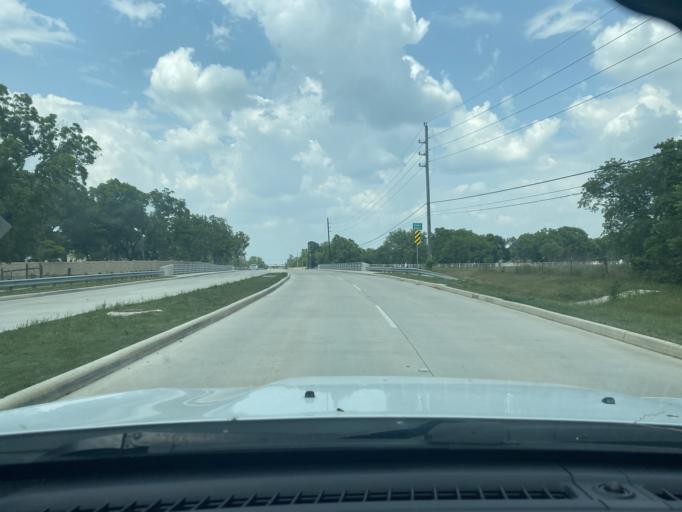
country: US
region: Texas
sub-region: Fort Bend County
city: Greatwood
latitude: 29.5449
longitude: -95.7227
